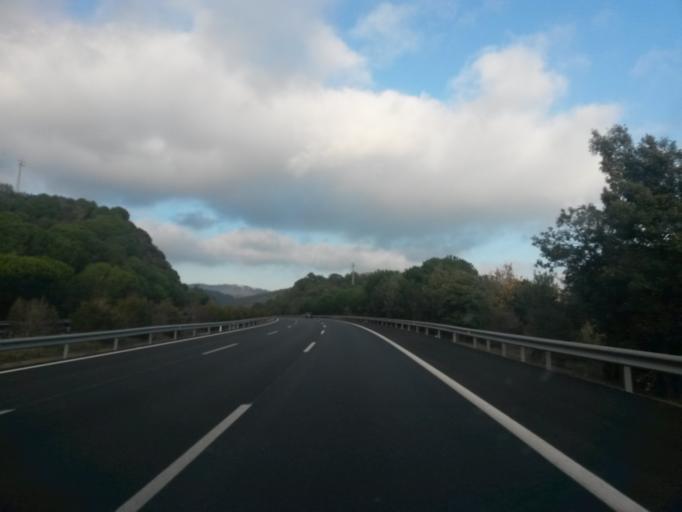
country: ES
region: Catalonia
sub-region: Provincia de Barcelona
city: Calella
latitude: 41.6328
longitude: 2.6695
